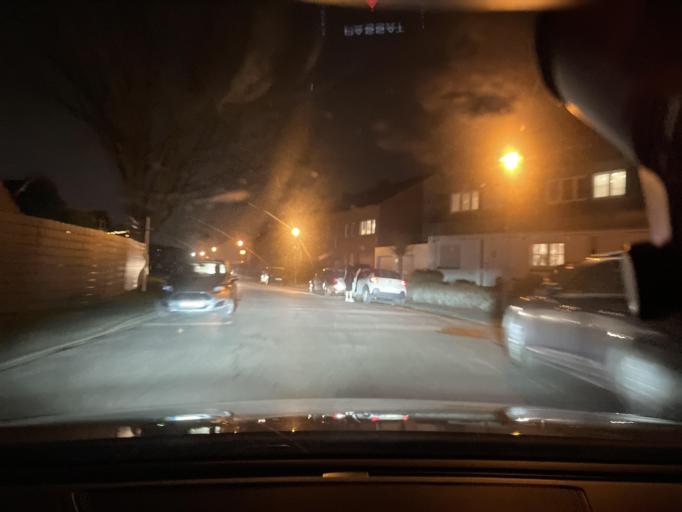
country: DE
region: North Rhine-Westphalia
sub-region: Regierungsbezirk Dusseldorf
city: Monchengladbach
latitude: 51.2264
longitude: 6.4690
